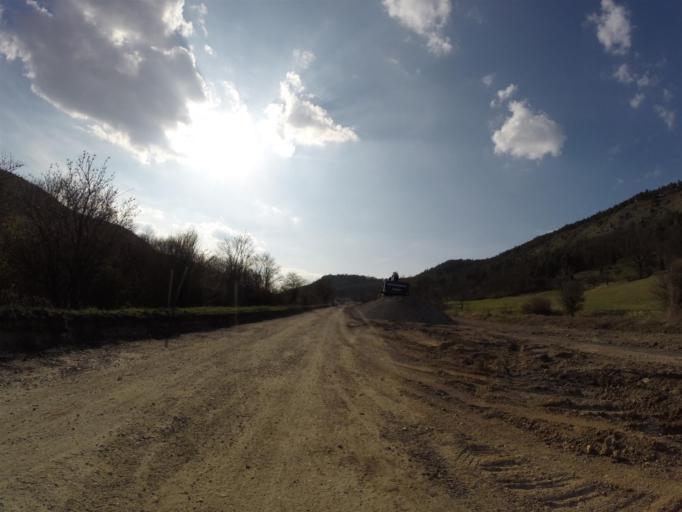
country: DE
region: Thuringia
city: Rothenstein
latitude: 50.8707
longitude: 11.5731
